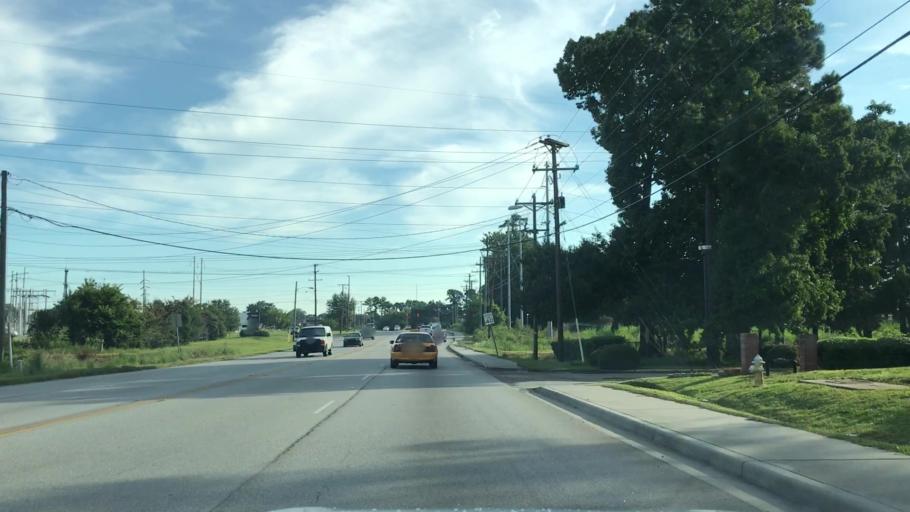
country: US
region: South Carolina
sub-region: Charleston County
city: North Charleston
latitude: 32.8478
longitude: -80.0139
